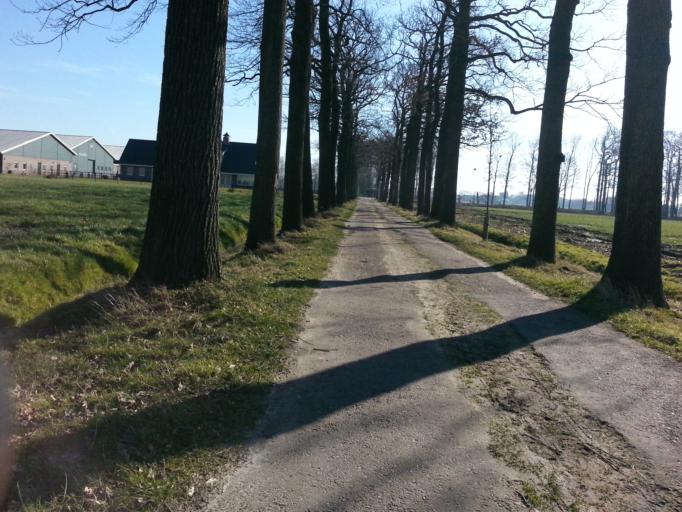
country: NL
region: Utrecht
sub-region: Gemeente Woudenberg
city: Woudenberg
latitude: 52.0859
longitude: 5.4358
